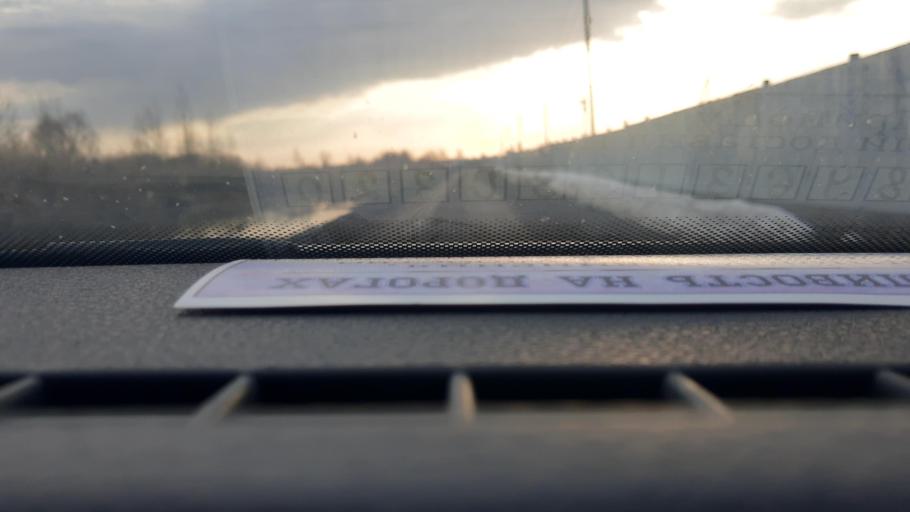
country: RU
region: Bashkortostan
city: Mikhaylovka
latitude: 54.7395
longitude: 55.8126
